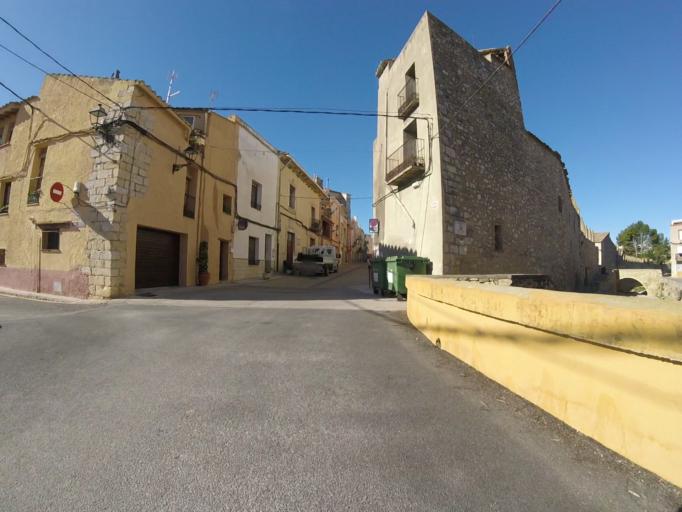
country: ES
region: Valencia
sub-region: Provincia de Castello
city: Chert/Xert
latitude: 40.4659
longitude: 0.1817
